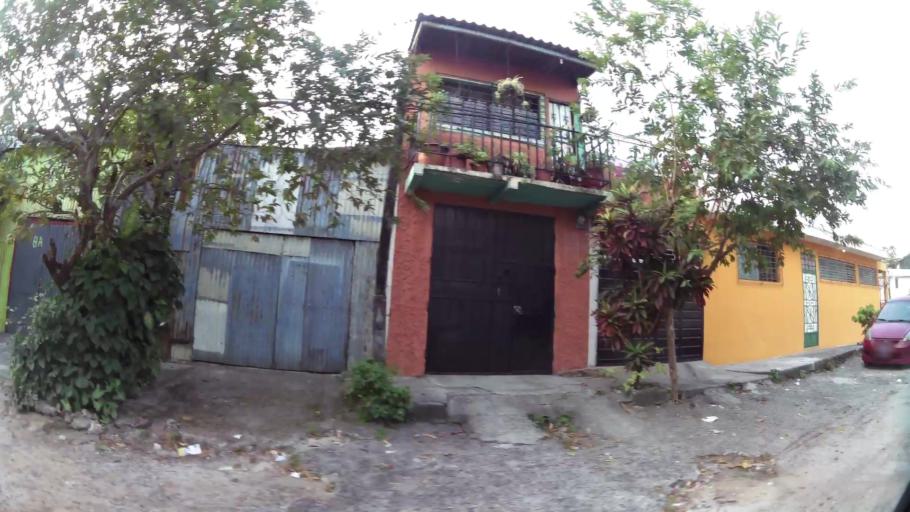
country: SV
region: San Salvador
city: San Salvador
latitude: 13.6924
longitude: -89.2044
